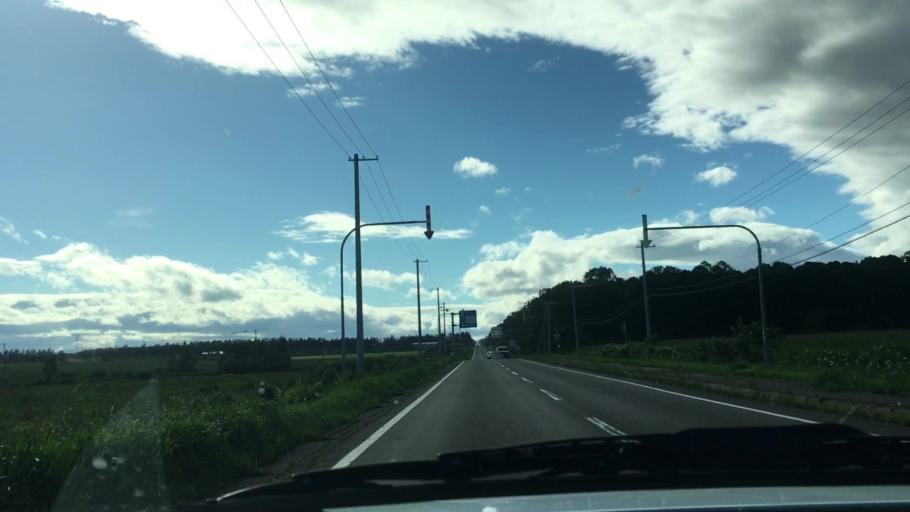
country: JP
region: Hokkaido
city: Otofuke
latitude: 43.1551
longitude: 143.1926
